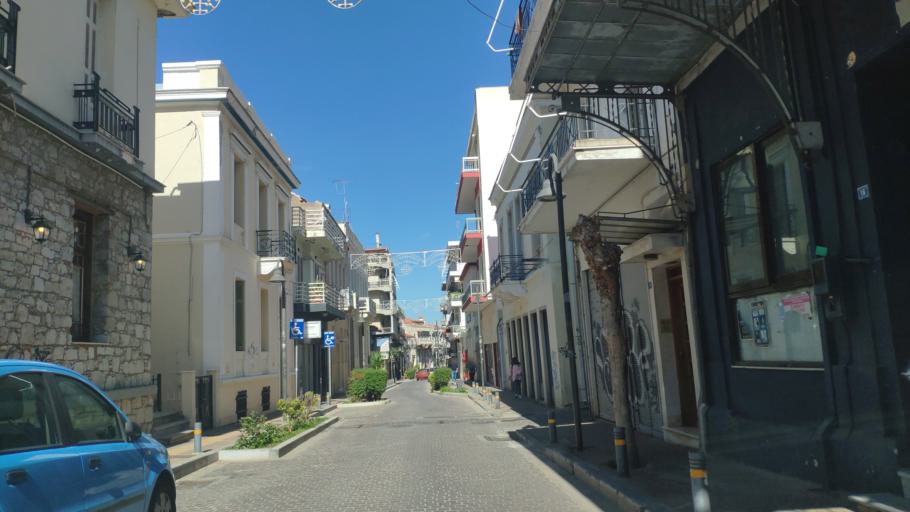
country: GR
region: Central Greece
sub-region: Nomos Voiotias
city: Livadeia
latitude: 38.4346
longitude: 22.8754
